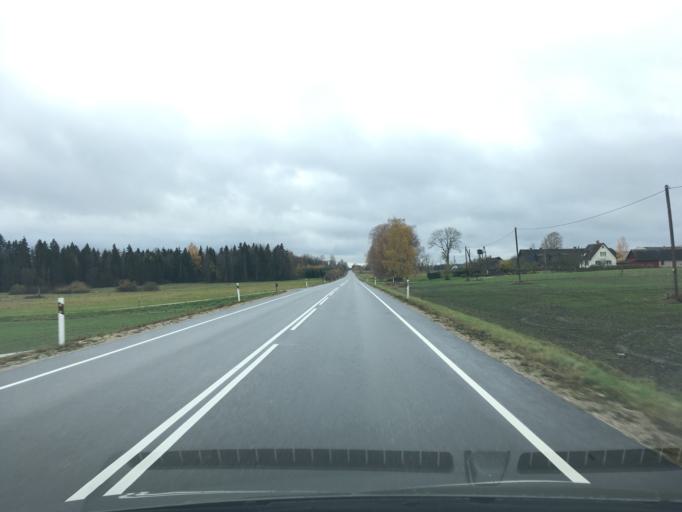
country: EE
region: Jogevamaa
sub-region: Tabivere vald
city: Tabivere
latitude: 58.4562
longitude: 26.5314
